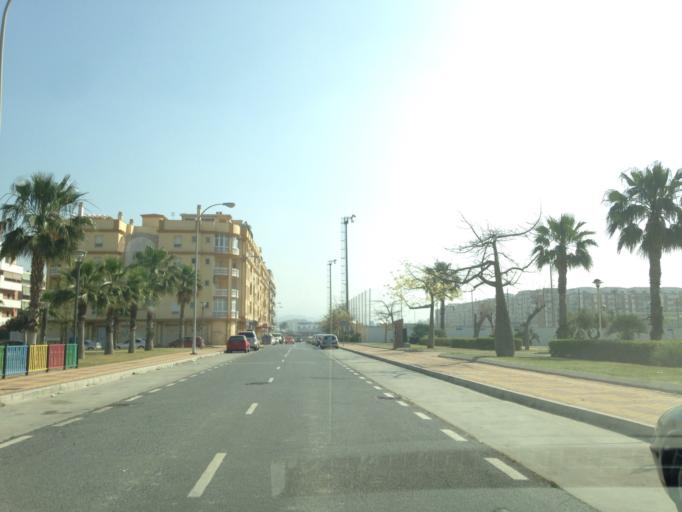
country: ES
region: Andalusia
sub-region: Provincia de Malaga
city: Malaga
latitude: 36.7012
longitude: -4.4571
